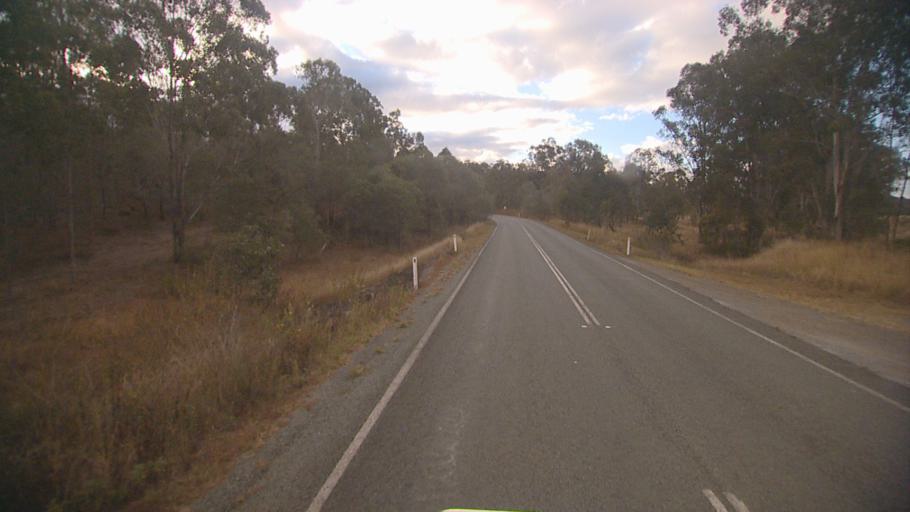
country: AU
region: Queensland
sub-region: Logan
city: Cedar Vale
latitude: -27.8955
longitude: 153.0880
